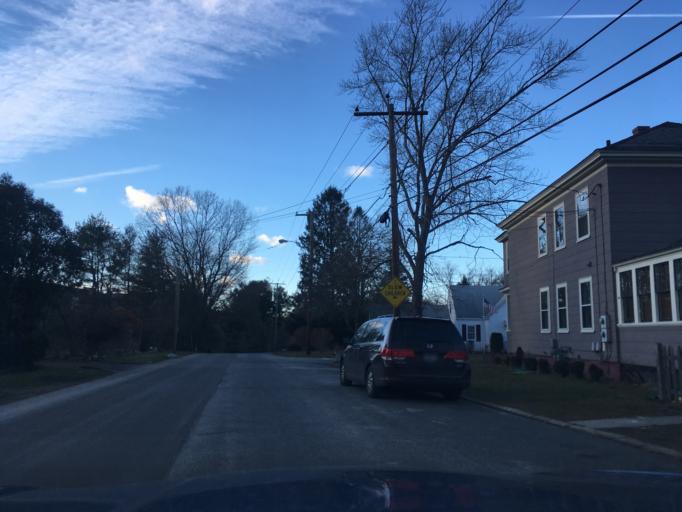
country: US
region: Rhode Island
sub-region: Kent County
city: East Greenwich
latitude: 41.6538
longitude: -71.4597
